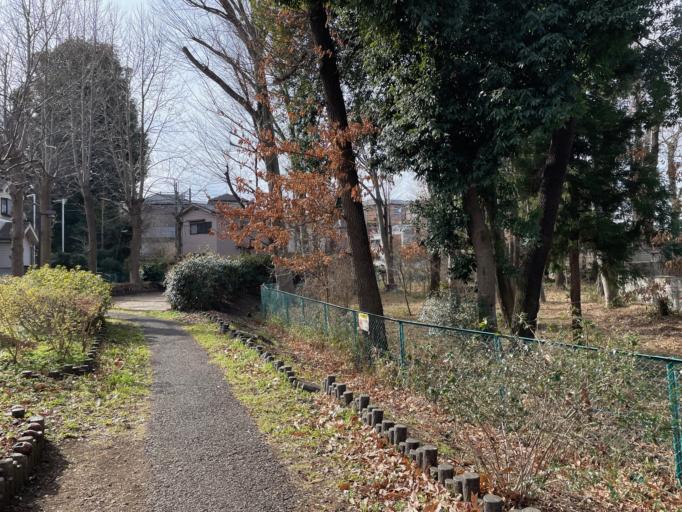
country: JP
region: Saitama
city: Tokorozawa
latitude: 35.7768
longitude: 139.5056
